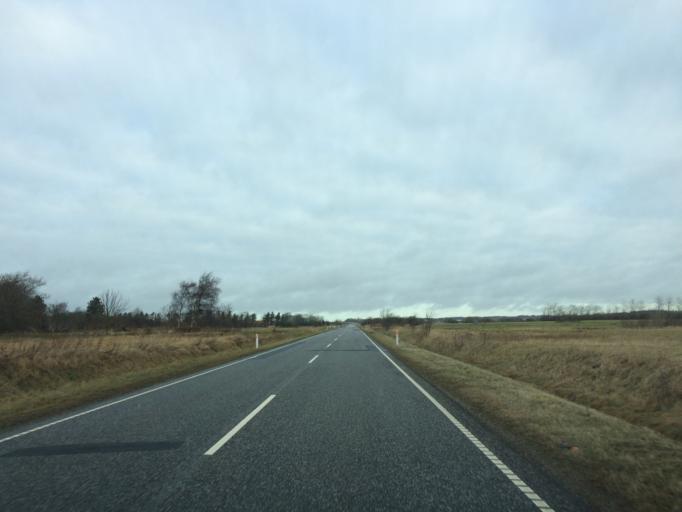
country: DK
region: Central Jutland
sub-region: Struer Kommune
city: Struer
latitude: 56.3948
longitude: 8.4585
